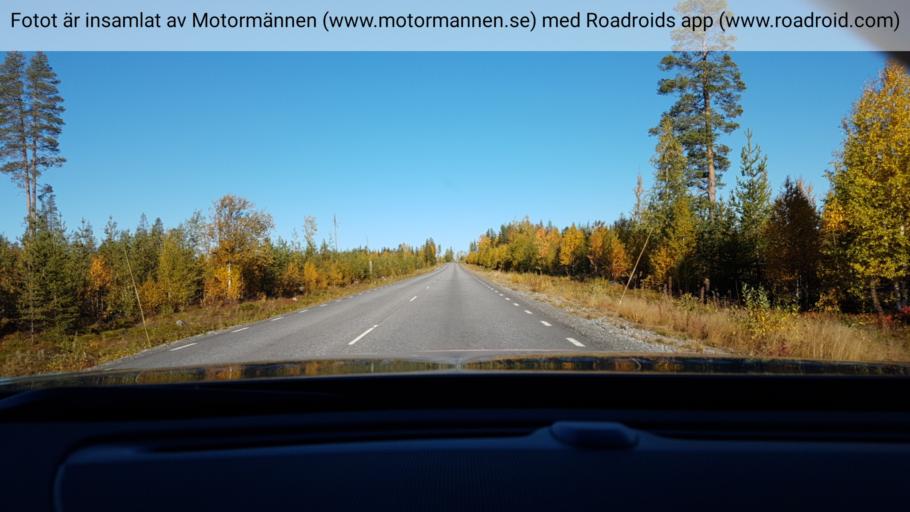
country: SE
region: Vaesterbotten
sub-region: Skelleftea Kommun
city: Storvik
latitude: 65.3462
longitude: 20.5075
